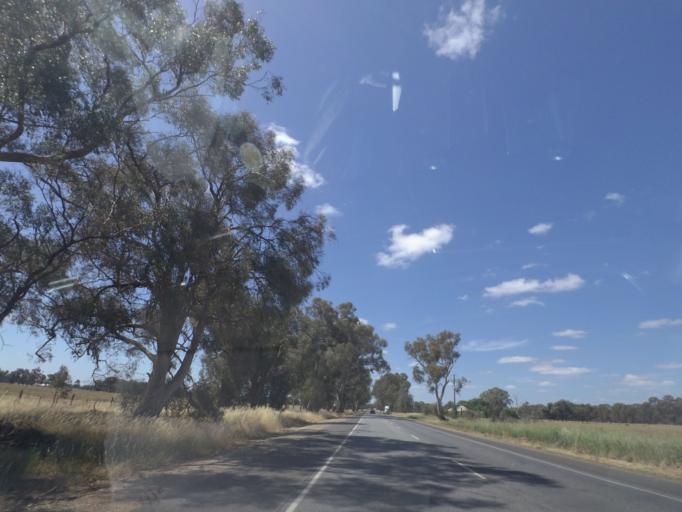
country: AU
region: Victoria
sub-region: Wangaratta
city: Wangaratta
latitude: -36.4033
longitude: 146.2749
